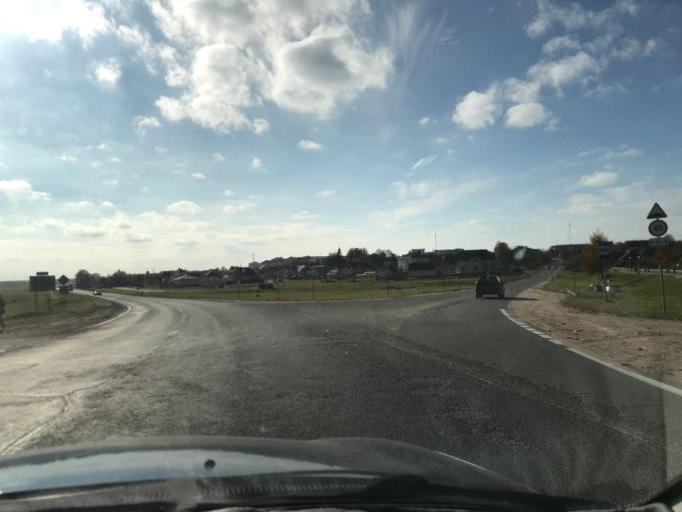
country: BY
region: Grodnenskaya
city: Voranava
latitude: 54.1574
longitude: 25.3259
